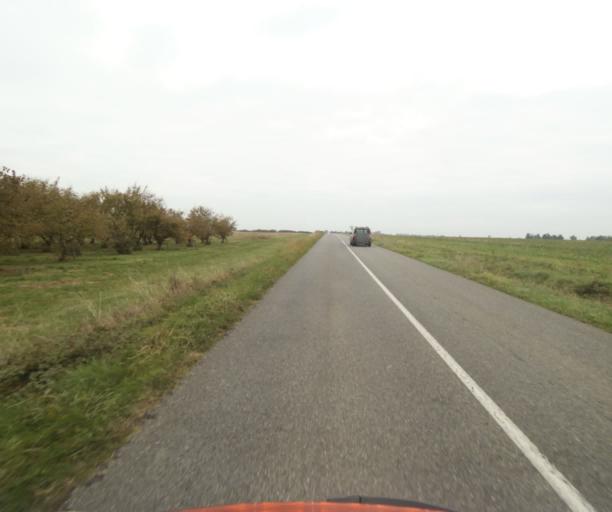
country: FR
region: Midi-Pyrenees
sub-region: Departement du Tarn-et-Garonne
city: Verdun-sur-Garonne
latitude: 43.8174
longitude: 1.1893
